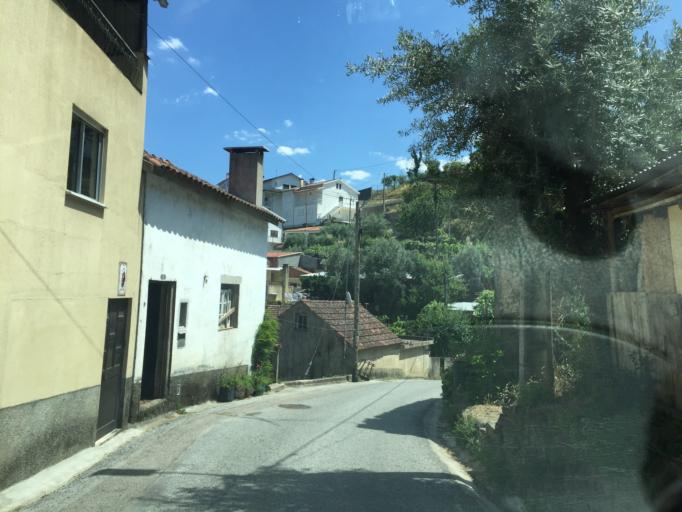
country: PT
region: Coimbra
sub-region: Pampilhosa da Serra
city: Pampilhosa da Serra
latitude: 40.0454
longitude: -7.9536
